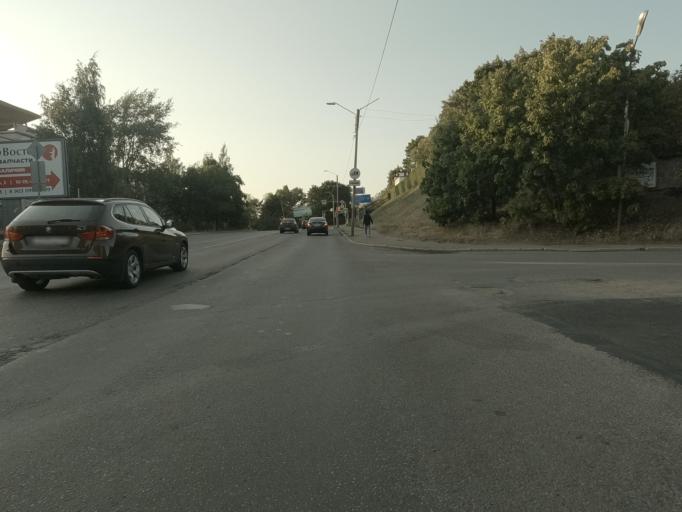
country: RU
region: Leningrad
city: Vyborg
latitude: 60.7130
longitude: 28.7573
